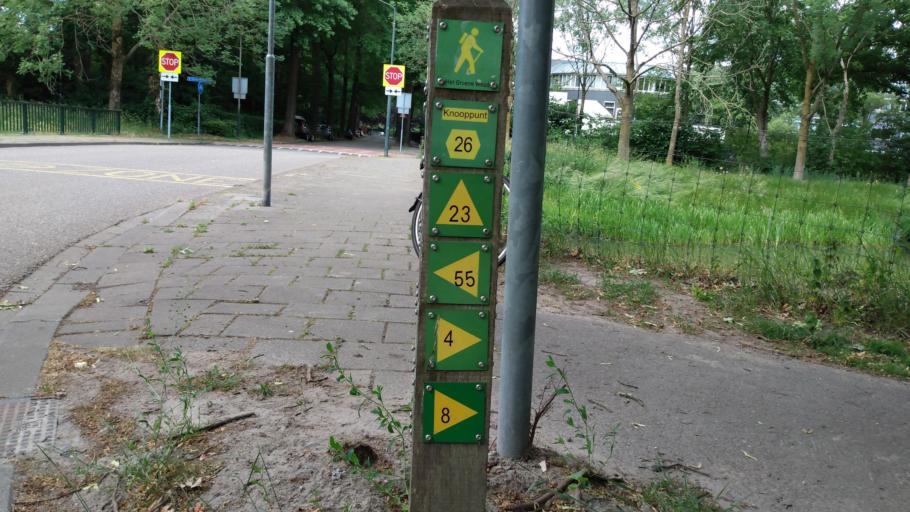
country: NL
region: North Brabant
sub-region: Gemeente Oisterwijk
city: Oisterwijk
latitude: 51.5754
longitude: 5.1856
